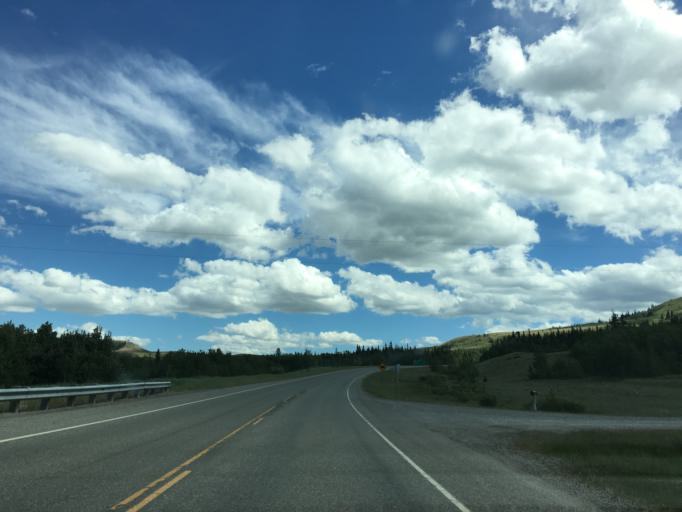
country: US
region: Montana
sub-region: Glacier County
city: Browning
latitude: 48.6083
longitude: -113.2868
